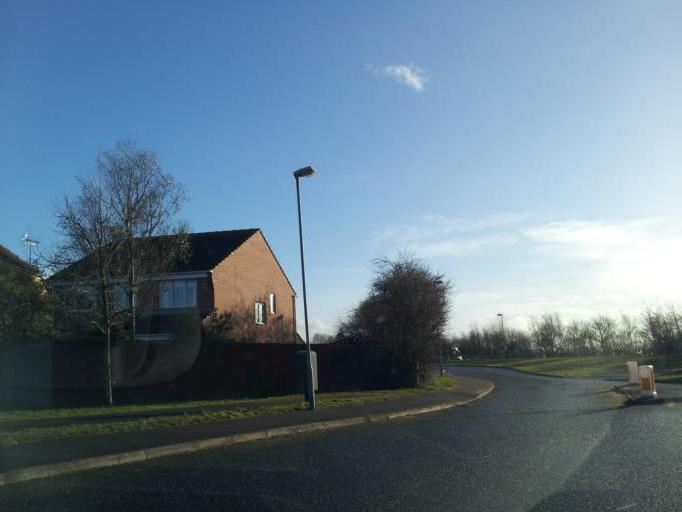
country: GB
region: England
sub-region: Nottinghamshire
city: Newark on Trent
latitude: 53.0733
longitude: -0.7721
